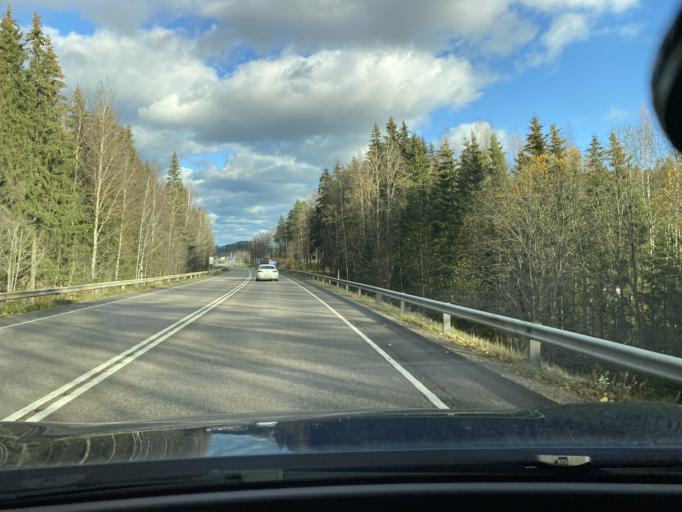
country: FI
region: Haeme
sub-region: Riihimaeki
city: Oitti
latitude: 60.7924
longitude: 25.0044
